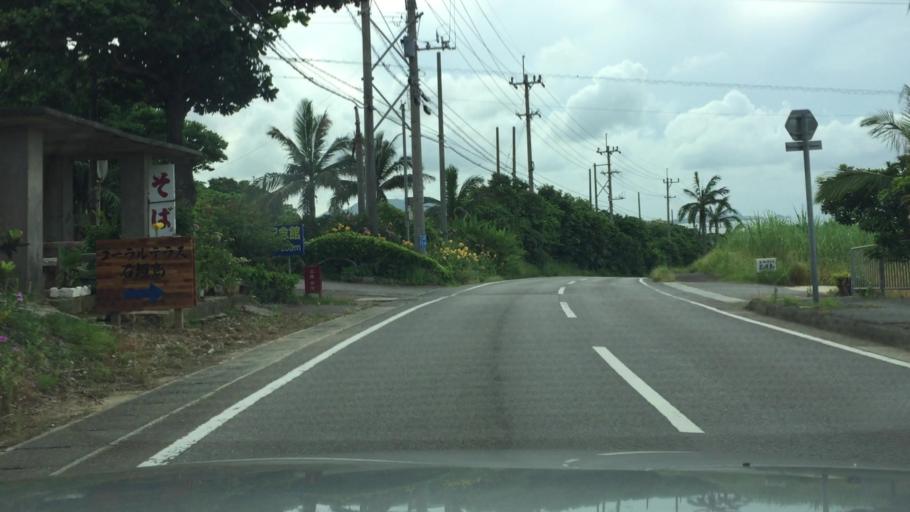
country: JP
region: Okinawa
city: Ishigaki
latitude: 24.4539
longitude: 124.1930
